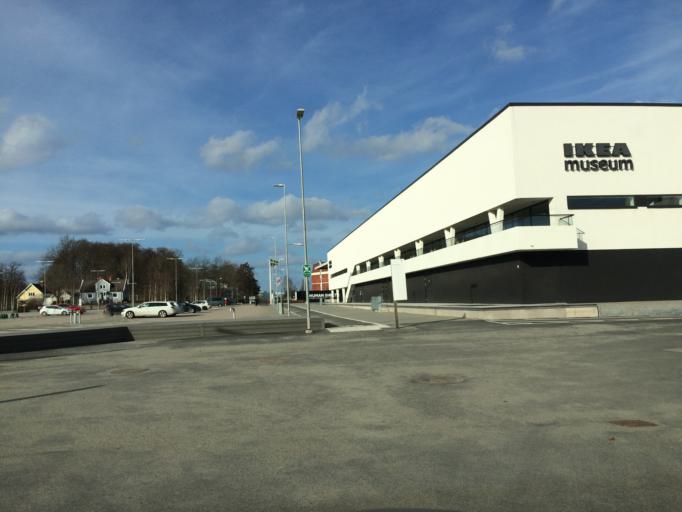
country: SE
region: Kronoberg
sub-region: Almhults Kommun
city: AElmhult
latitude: 56.5514
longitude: 14.1337
